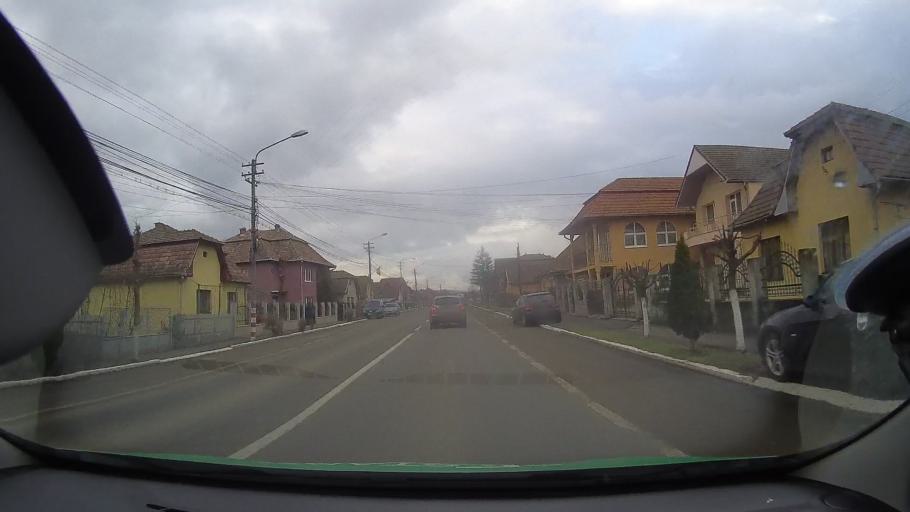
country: RO
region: Cluj
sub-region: Municipiul Campia Turzii
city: Campia Turzii
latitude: 46.5328
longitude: 23.8989
